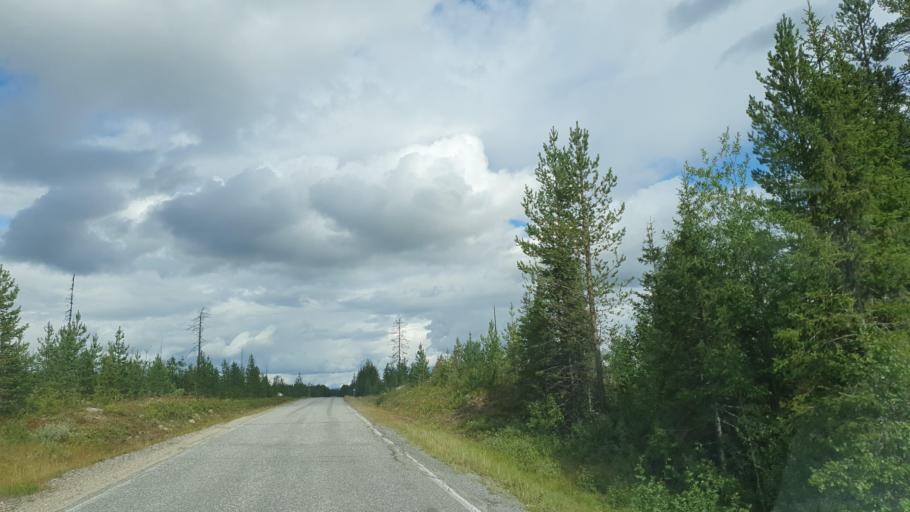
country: FI
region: Lapland
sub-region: Tunturi-Lappi
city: Muonio
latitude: 67.8140
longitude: 24.0676
